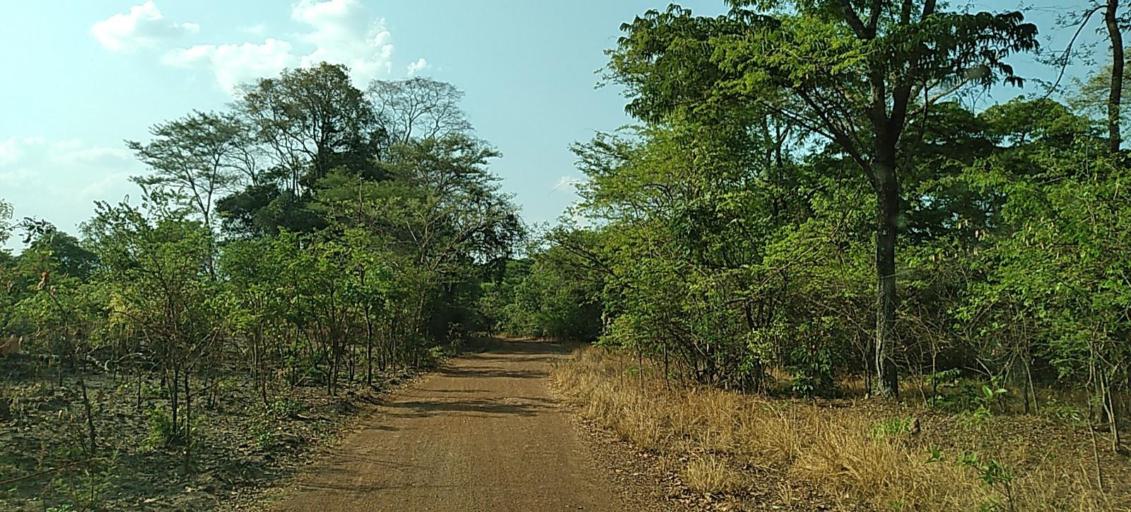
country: ZM
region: Copperbelt
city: Mpongwe
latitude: -13.4466
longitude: 28.0635
